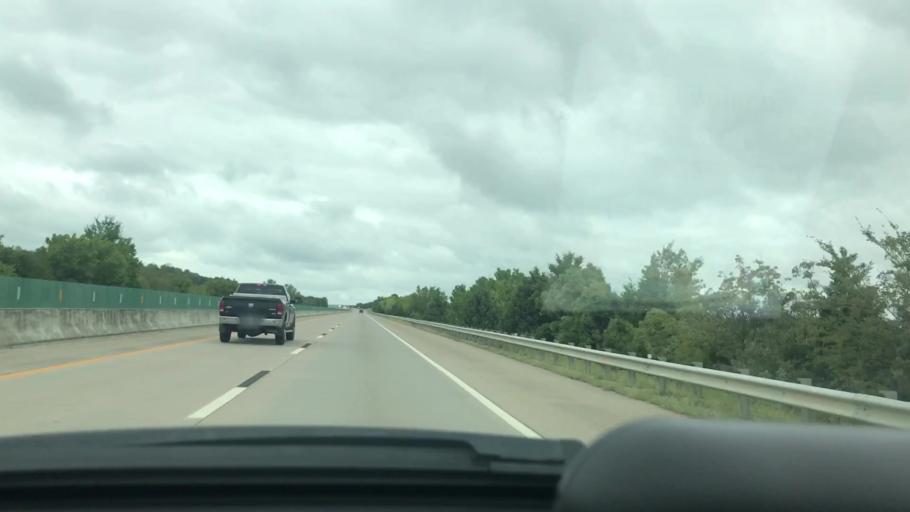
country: US
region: Oklahoma
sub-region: Pittsburg County
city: Krebs
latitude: 35.0258
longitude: -95.7154
